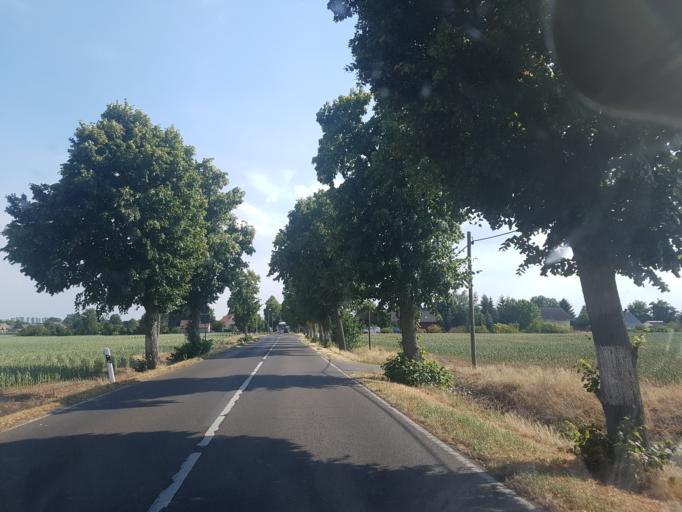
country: DE
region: Brandenburg
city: Trebbin
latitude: 52.1811
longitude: 13.2354
